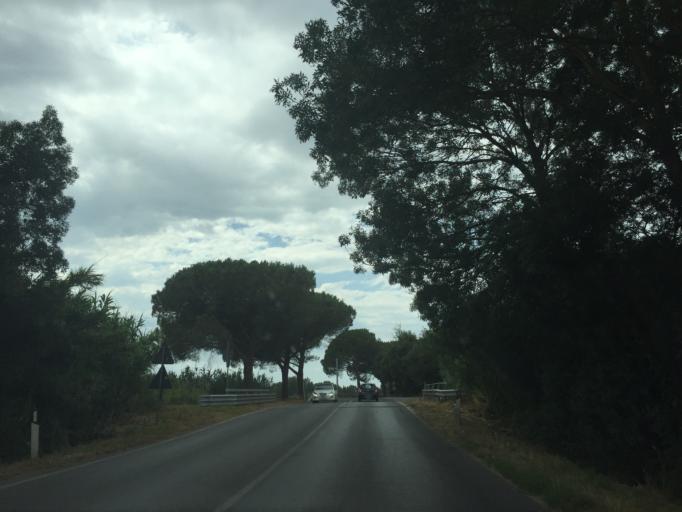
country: IT
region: Tuscany
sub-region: Province of Pisa
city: Asciano
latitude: 43.7504
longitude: 10.4549
